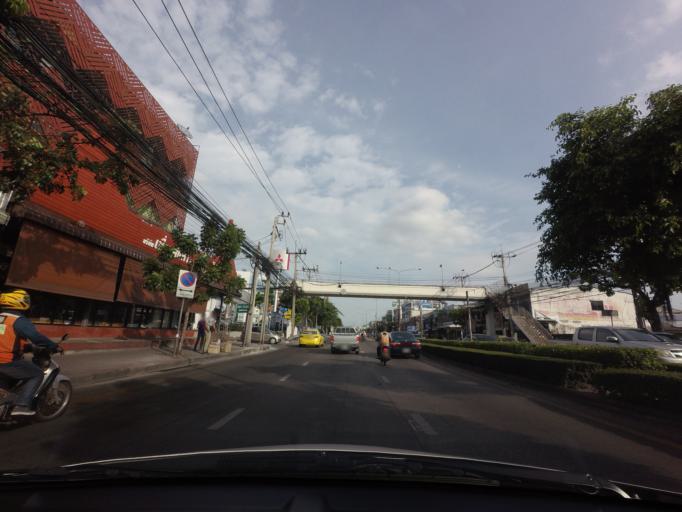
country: TH
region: Bangkok
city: Bueng Kum
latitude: 13.7972
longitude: 100.6504
